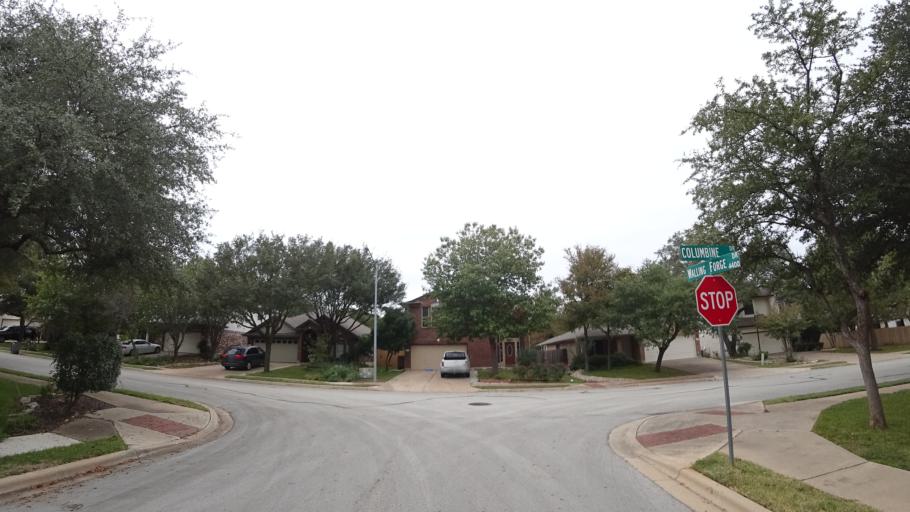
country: US
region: Texas
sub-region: Travis County
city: Wells Branch
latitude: 30.4288
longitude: -97.7183
